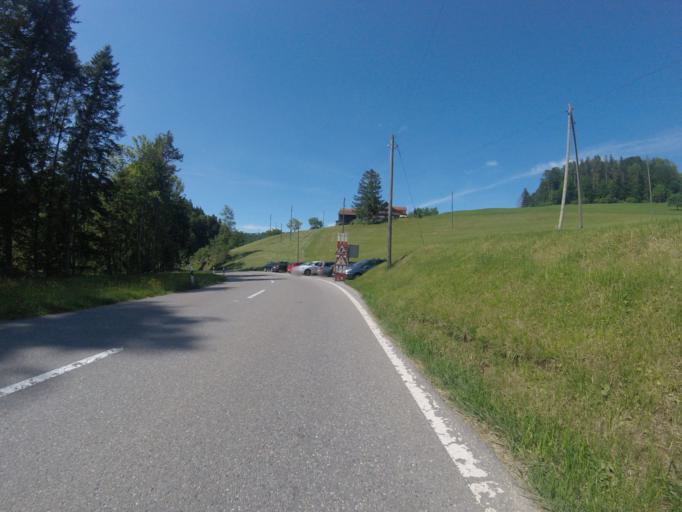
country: CH
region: Saint Gallen
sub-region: Wahlkreis Toggenburg
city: Mogelsberg
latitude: 47.3710
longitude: 9.1225
